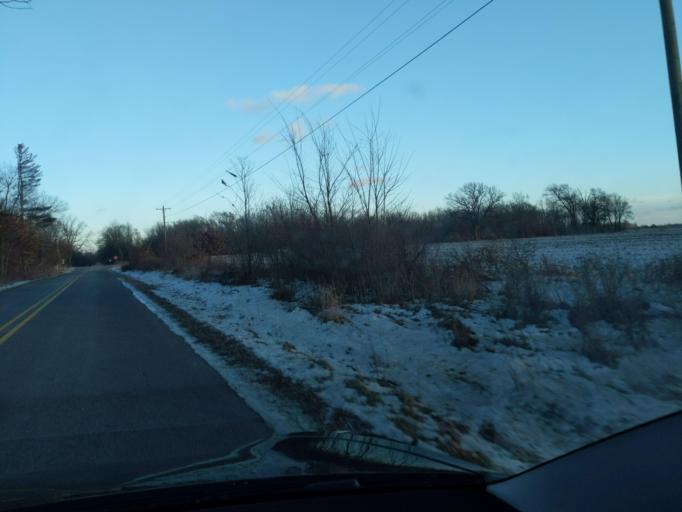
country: US
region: Michigan
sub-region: Ingham County
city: Stockbridge
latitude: 42.4540
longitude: -84.2117
